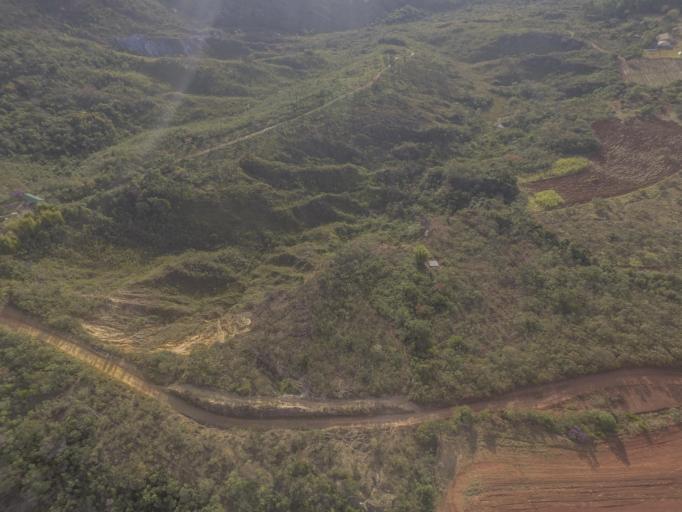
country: BR
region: Minas Gerais
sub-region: Tiradentes
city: Tiradentes
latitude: -21.0584
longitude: -44.1002
